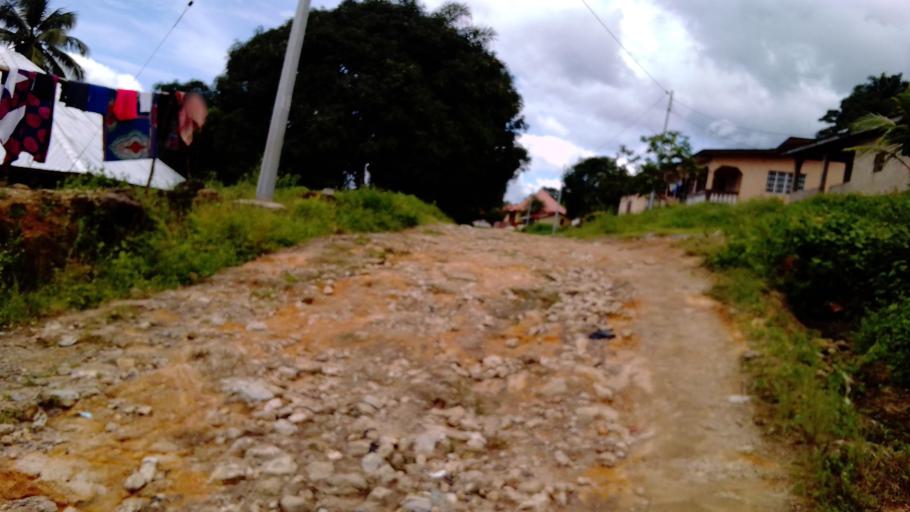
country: SL
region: Eastern Province
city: Koyima
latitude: 8.6986
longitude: -11.0093
